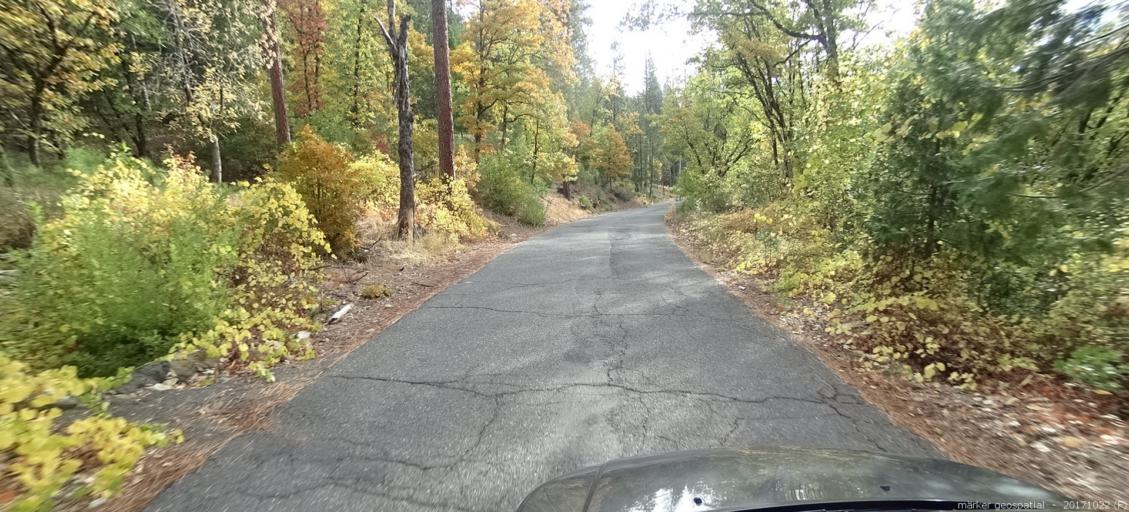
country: US
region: California
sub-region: Siskiyou County
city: Dunsmuir
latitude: 41.1555
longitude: -122.3465
